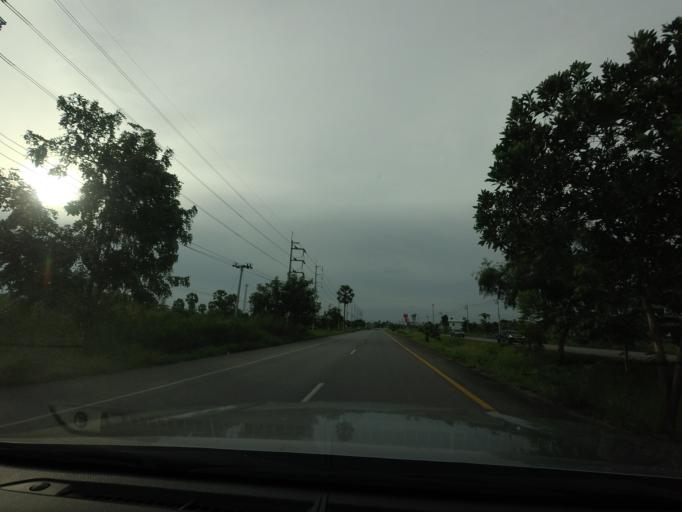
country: TH
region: Nakhon Si Thammarat
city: Hua Sai
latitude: 8.0412
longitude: 100.2879
